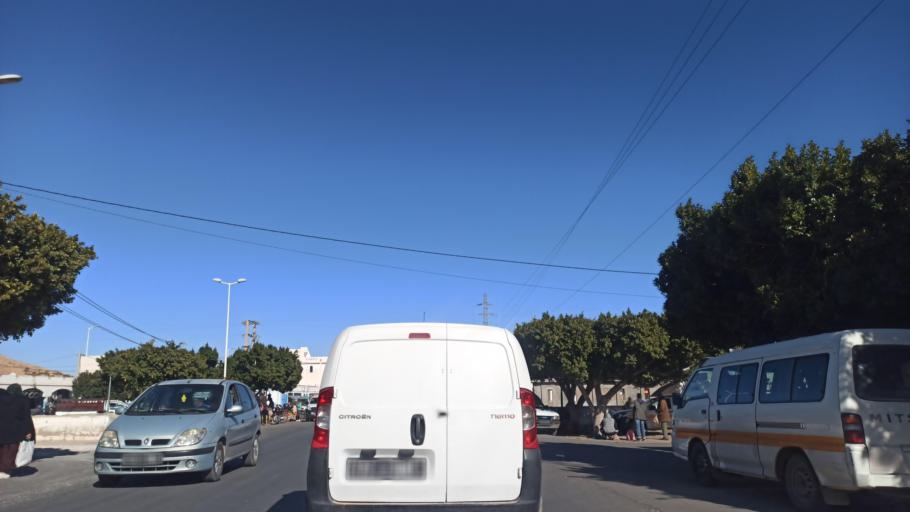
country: TN
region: Sidi Bu Zayd
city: Bi'r al Hufayy
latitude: 34.9298
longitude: 9.1941
